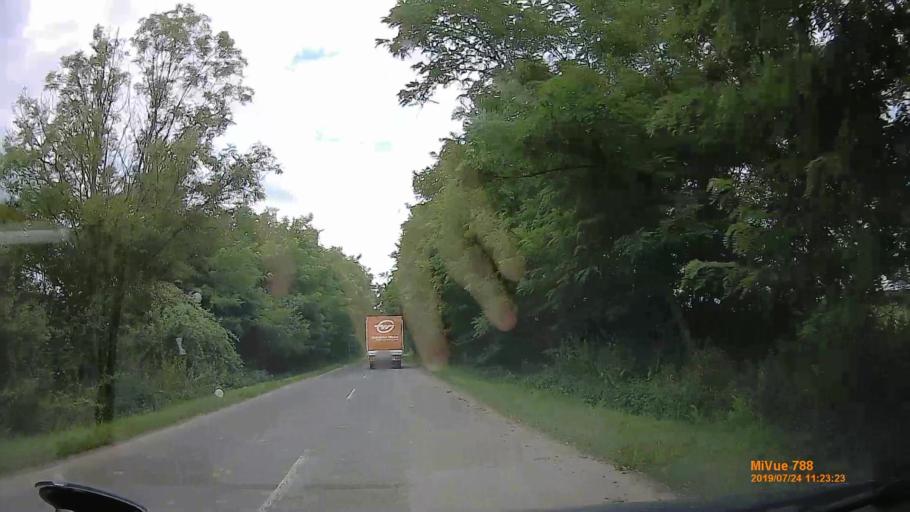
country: HU
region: Szabolcs-Szatmar-Bereg
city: Tarpa
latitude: 48.1894
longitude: 22.4591
